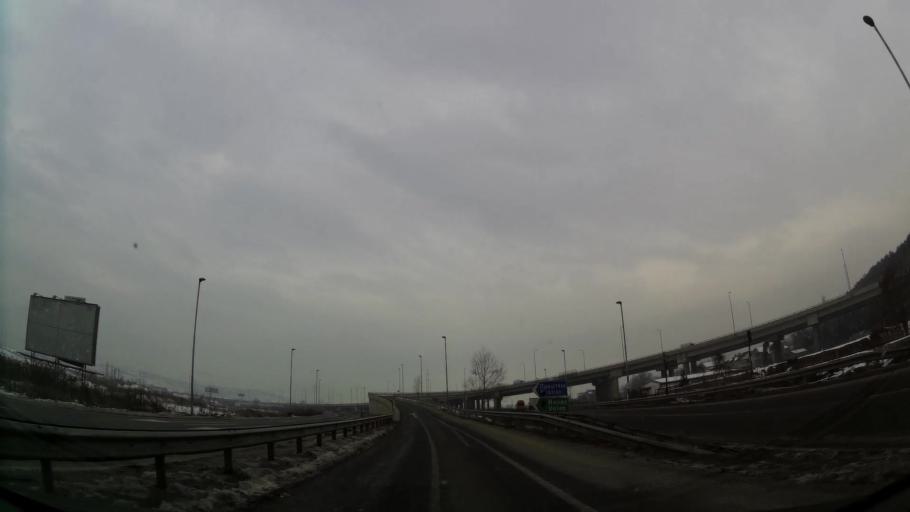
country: MK
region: Saraj
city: Saraj
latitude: 42.0086
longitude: 21.3253
